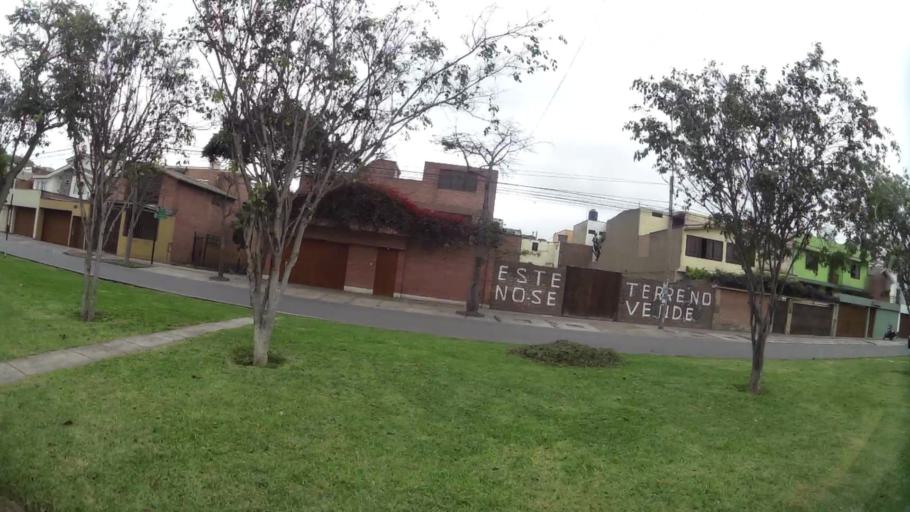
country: PE
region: Lima
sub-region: Lima
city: La Molina
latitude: -12.0668
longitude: -76.9645
